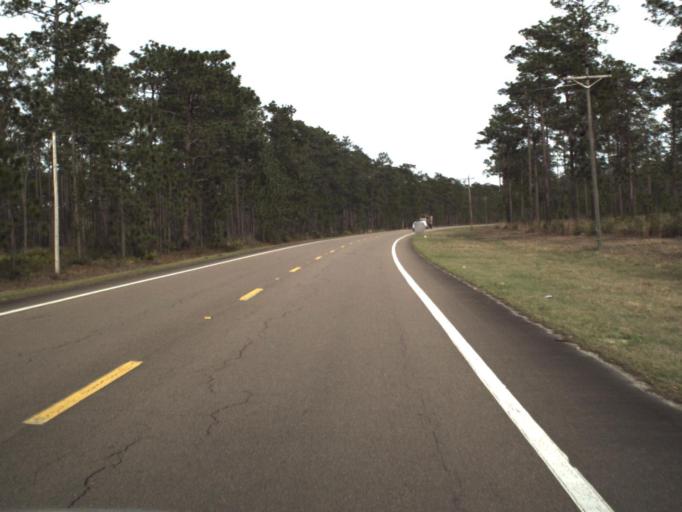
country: US
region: Florida
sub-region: Gulf County
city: Wewahitchka
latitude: 30.1450
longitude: -85.3215
